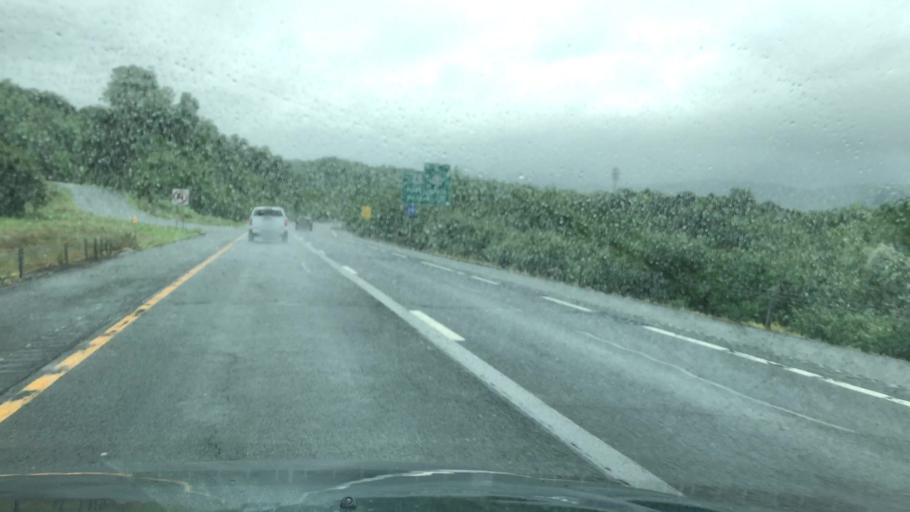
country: US
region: New York
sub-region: Orange County
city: Port Jervis
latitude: 41.3552
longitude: -74.6733
